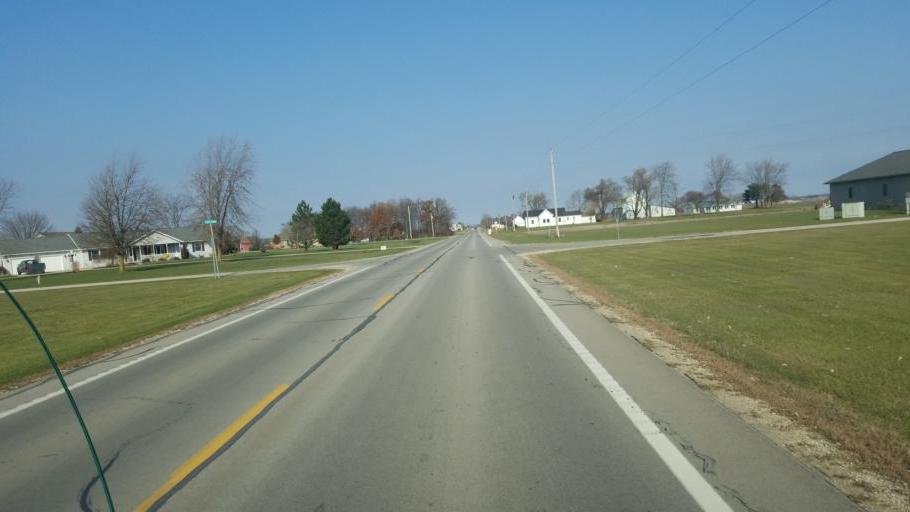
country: US
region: Ohio
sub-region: Mercer County
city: Coldwater
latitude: 40.5231
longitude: -84.6286
